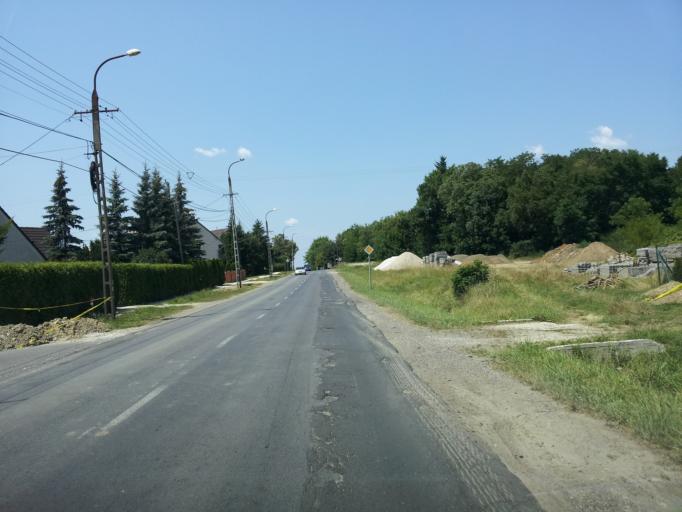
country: HU
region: Zala
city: Zalaegerszeg
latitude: 46.8769
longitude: 16.7421
